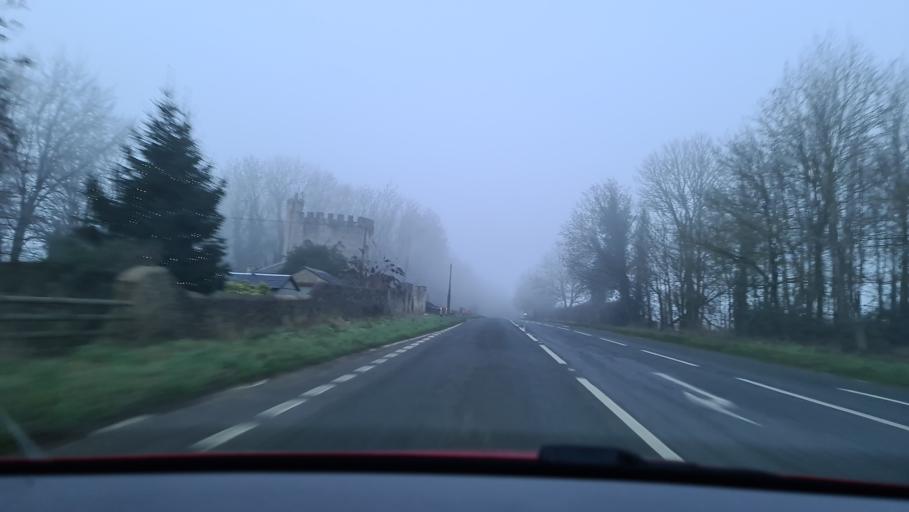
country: GB
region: England
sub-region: Oxfordshire
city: Bicester
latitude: 51.8948
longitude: -1.2261
